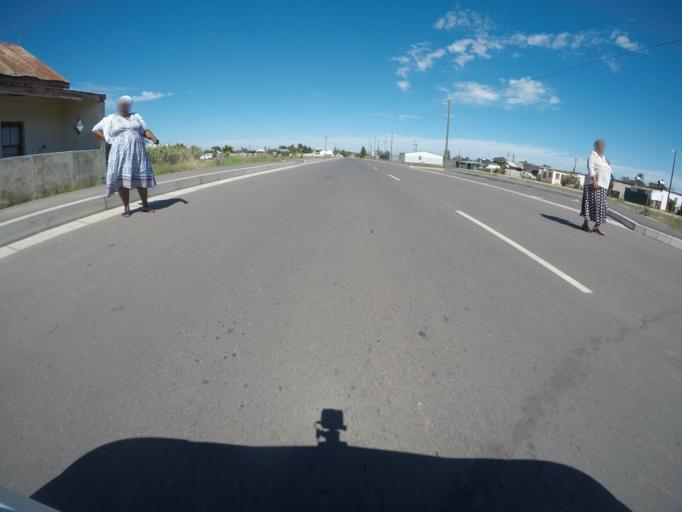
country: ZA
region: Western Cape
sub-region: West Coast District Municipality
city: Malmesbury
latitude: -33.5742
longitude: 18.6470
